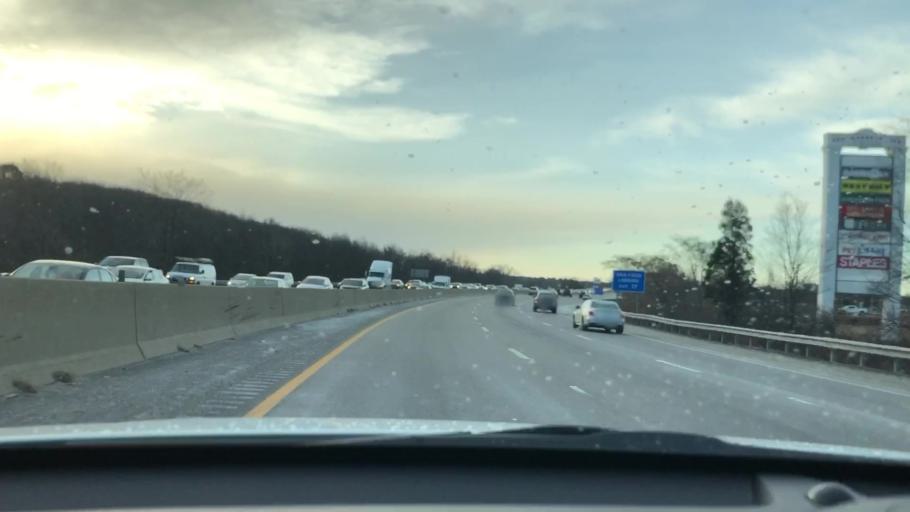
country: US
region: Massachusetts
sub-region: Norfolk County
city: Braintree
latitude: 42.2162
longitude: -70.9975
